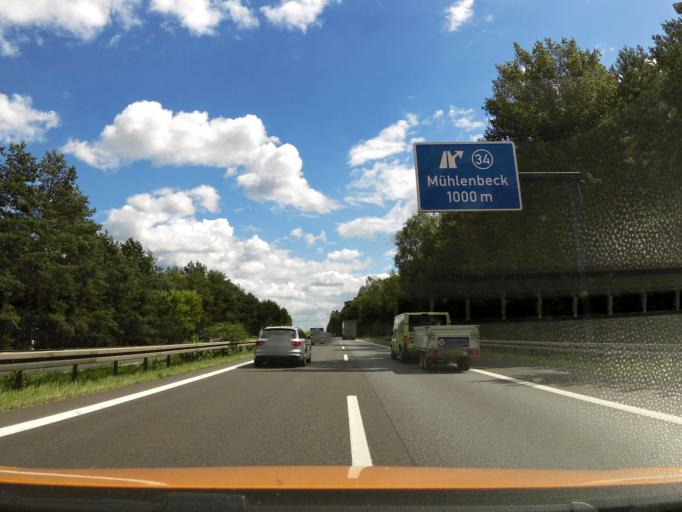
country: DE
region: Brandenburg
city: Glienicke
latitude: 52.6823
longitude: 13.3503
